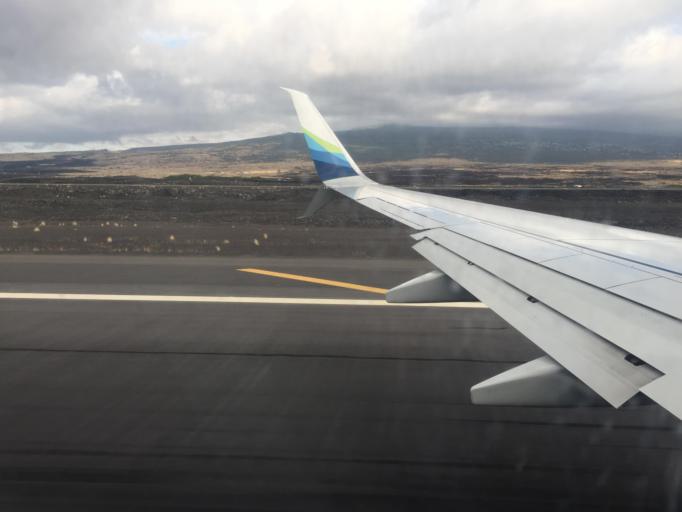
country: US
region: Hawaii
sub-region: Hawaii County
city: Kalaoa
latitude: 19.7473
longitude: -156.0449
